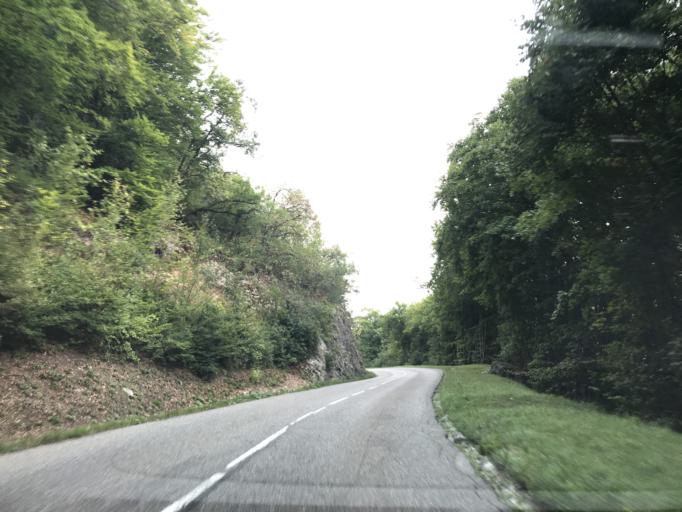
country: FR
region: Rhone-Alpes
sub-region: Departement de la Haute-Savoie
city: Talloires
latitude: 45.8481
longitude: 6.2197
